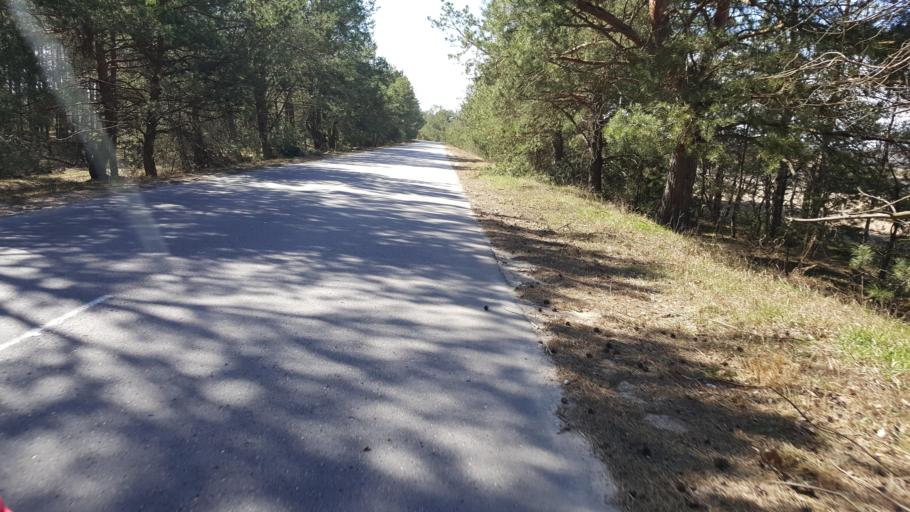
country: BY
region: Brest
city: Kamyanyets
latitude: 52.3073
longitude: 23.8637
